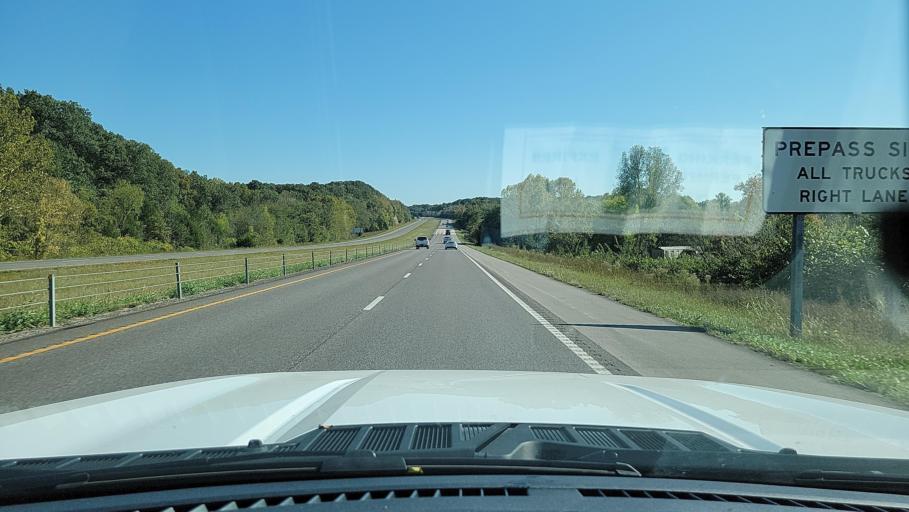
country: US
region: Missouri
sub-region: Jefferson County
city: Crystal City
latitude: 38.0425
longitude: -90.2639
